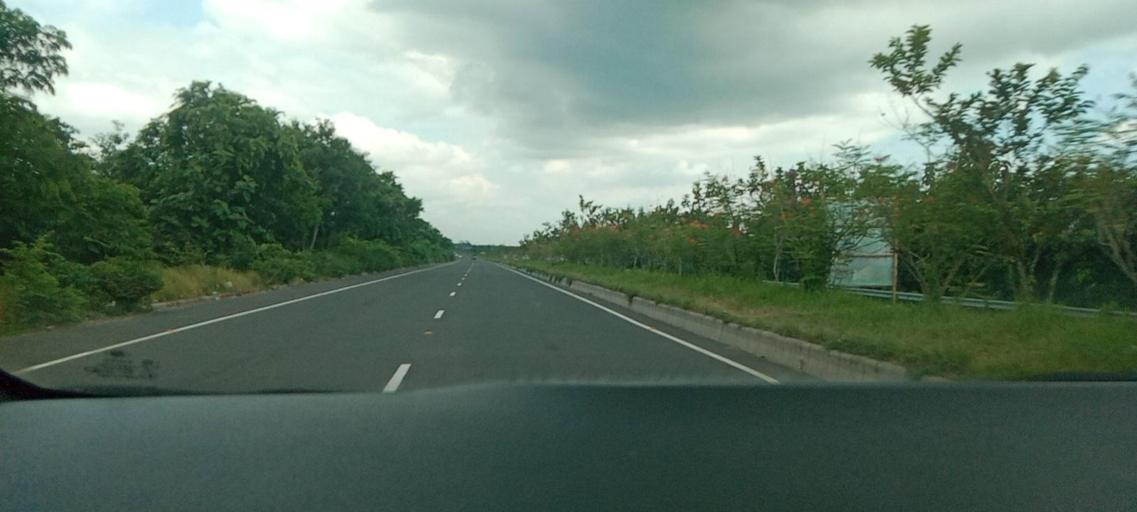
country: BD
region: Dhaka
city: Char Bhadrasan
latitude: 23.3985
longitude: 90.2218
